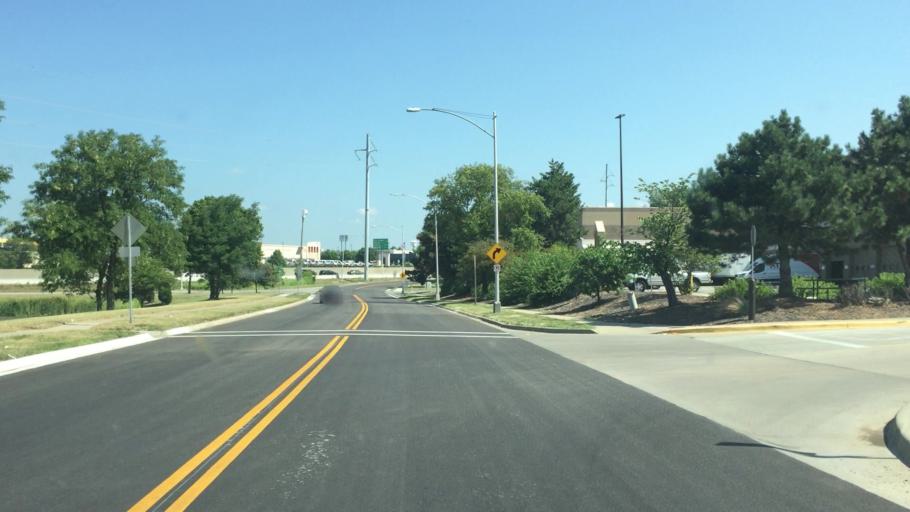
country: US
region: Kansas
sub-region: Johnson County
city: Lenexa
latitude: 38.9586
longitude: -94.7284
